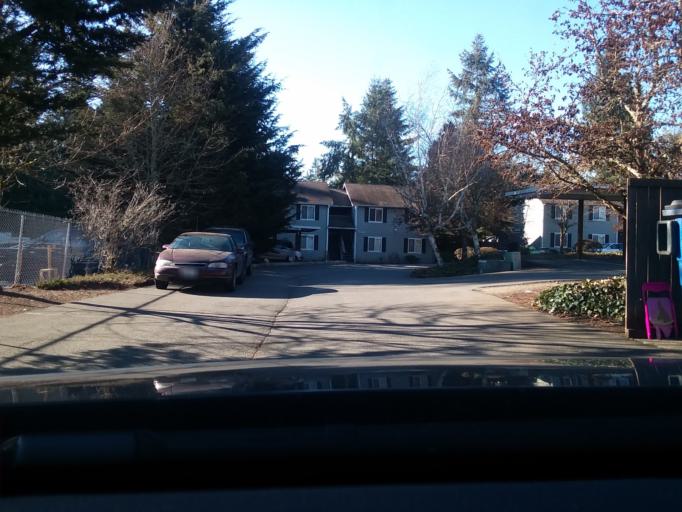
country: US
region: Washington
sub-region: Pierce County
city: Frederickson
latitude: 47.0954
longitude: -122.3156
